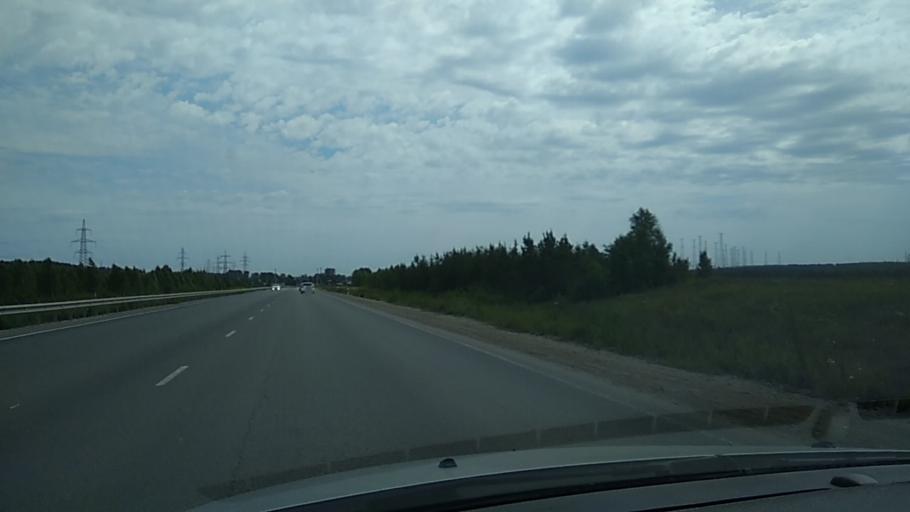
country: RU
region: Sverdlovsk
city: Verkhnyaya Pyshma
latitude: 56.9514
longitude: 60.5884
